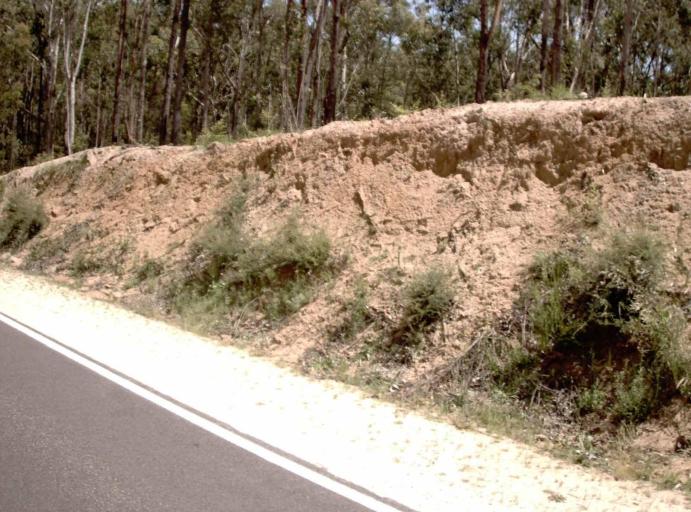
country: AU
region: New South Wales
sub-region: Bombala
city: Bombala
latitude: -37.5650
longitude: 149.2515
